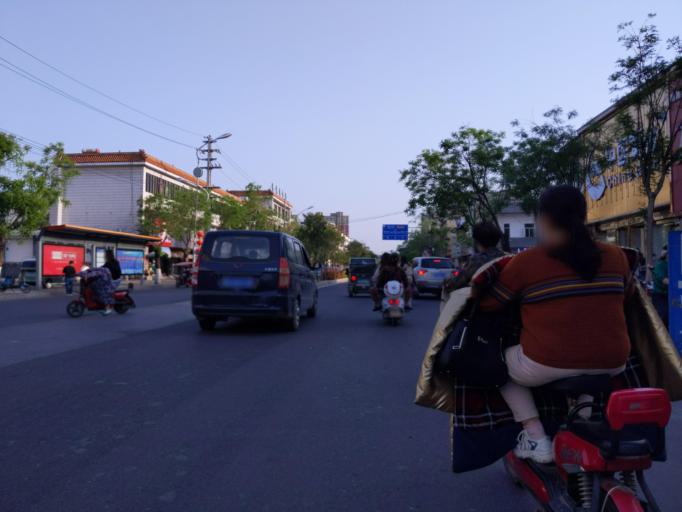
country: CN
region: Henan Sheng
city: Puyang Chengguanzhen
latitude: 35.7030
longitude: 115.0163
